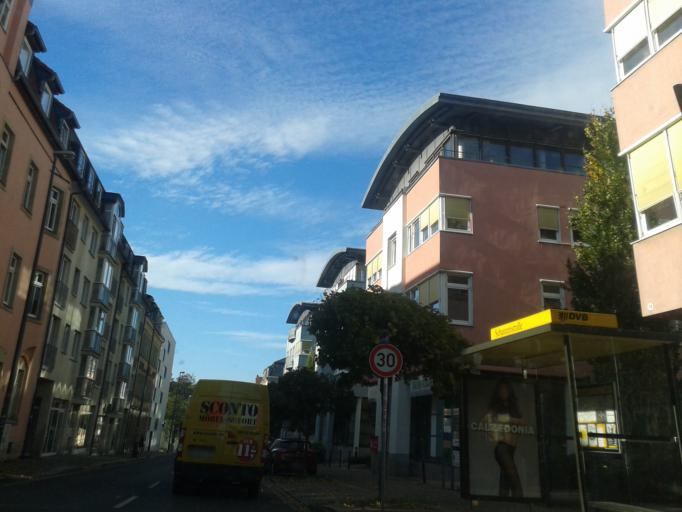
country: DE
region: Saxony
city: Albertstadt
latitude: 51.0775
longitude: 13.7501
